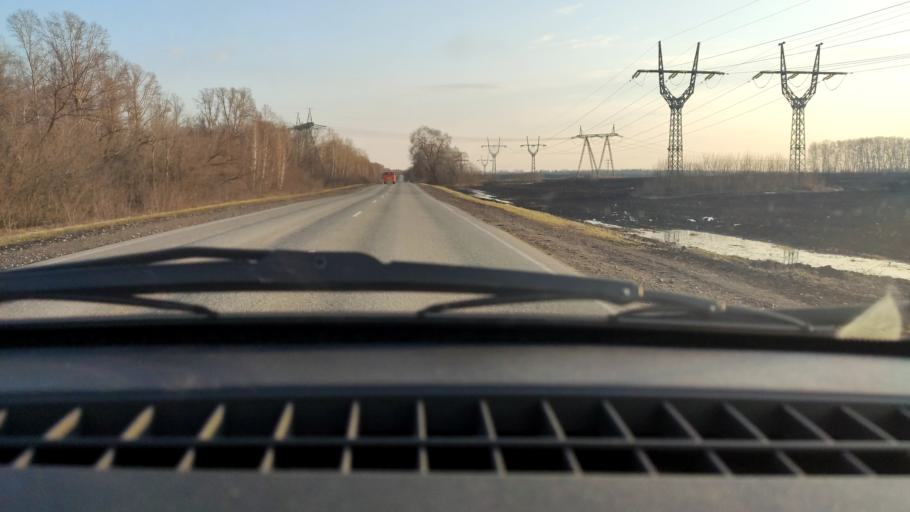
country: RU
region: Bashkortostan
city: Chishmy
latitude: 54.5202
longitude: 55.2976
